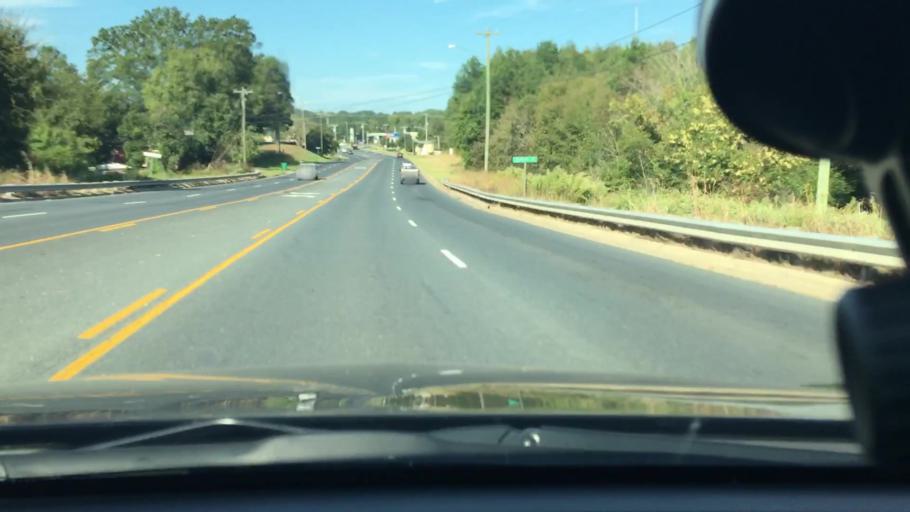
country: US
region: North Carolina
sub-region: Stanly County
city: Albemarle
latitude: 35.3852
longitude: -80.1874
